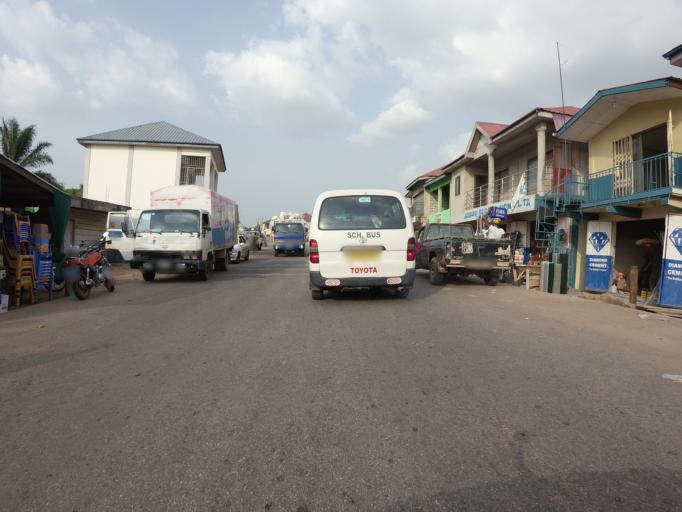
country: GH
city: Akropong
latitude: 6.2545
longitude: 0.1339
